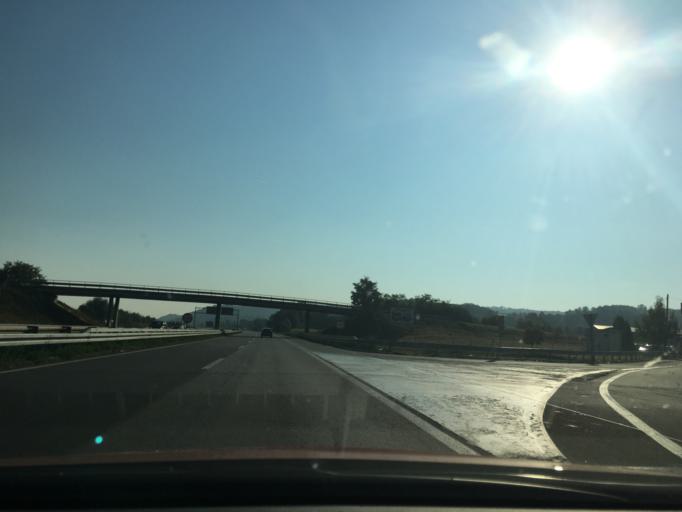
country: RS
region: Central Serbia
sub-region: Belgrade
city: Grocka
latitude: 44.5751
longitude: 20.7455
